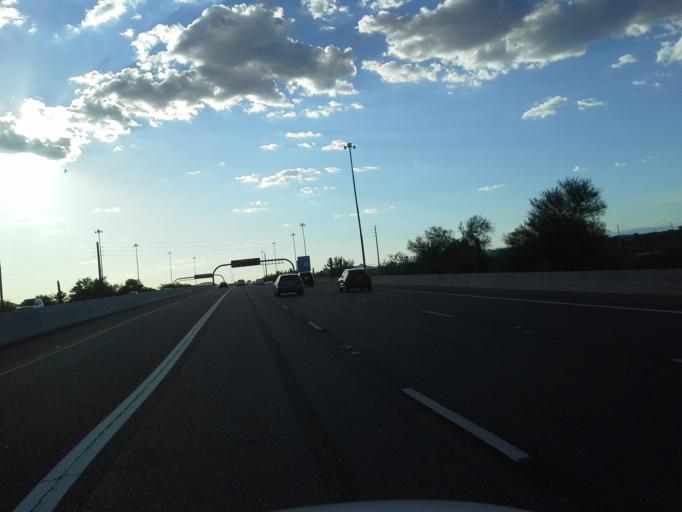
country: US
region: Arizona
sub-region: Maricopa County
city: Paradise Valley
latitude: 33.6666
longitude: -111.9571
